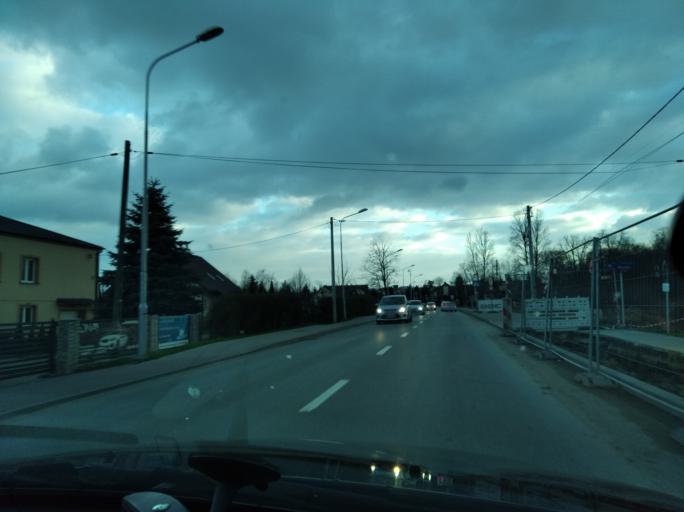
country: PL
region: Subcarpathian Voivodeship
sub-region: Rzeszow
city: Rzeszow
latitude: 50.0282
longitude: 22.0422
